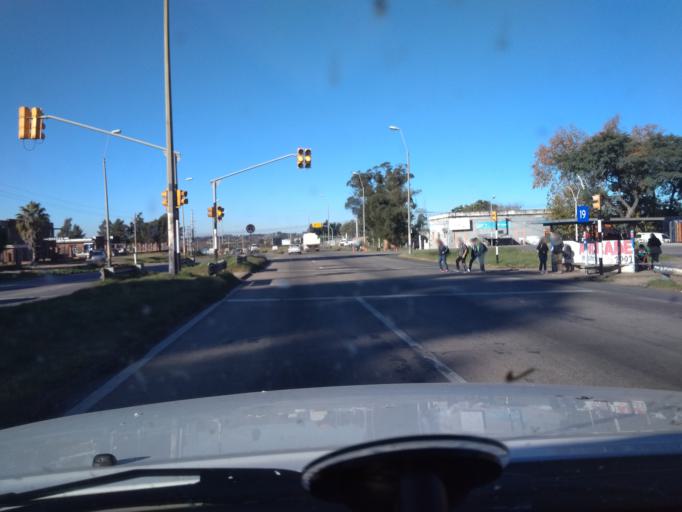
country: UY
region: Canelones
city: Colonia Nicolich
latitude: -34.7764
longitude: -56.0443
